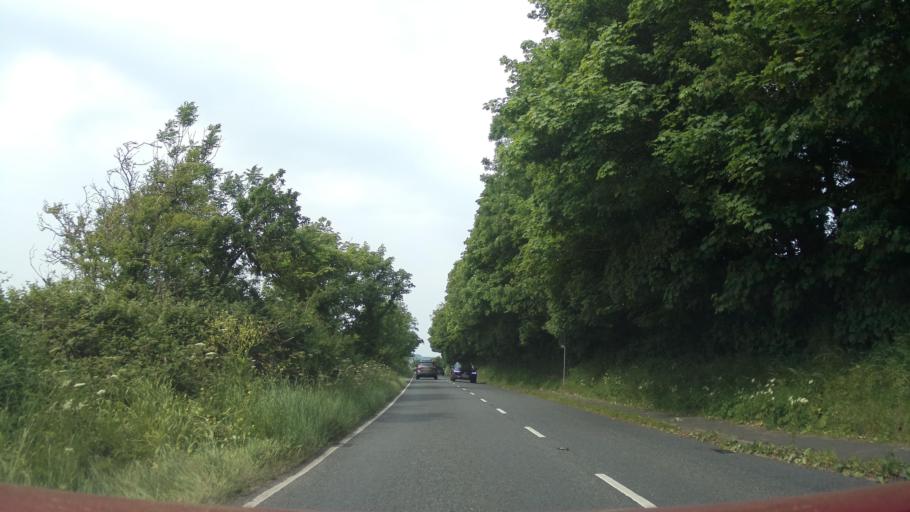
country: GB
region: England
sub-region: Devon
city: Colyton
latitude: 50.7070
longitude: -3.0580
